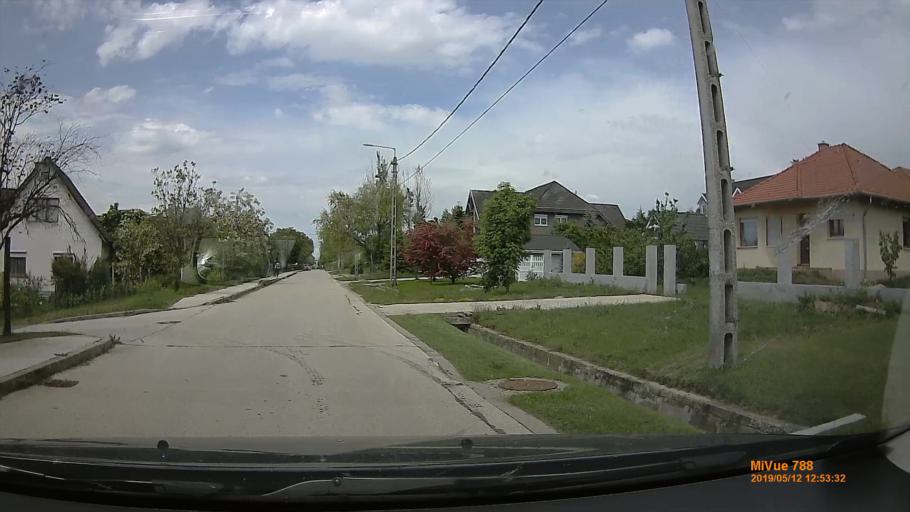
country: HU
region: Pest
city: Ecser
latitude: 47.4681
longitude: 19.3080
